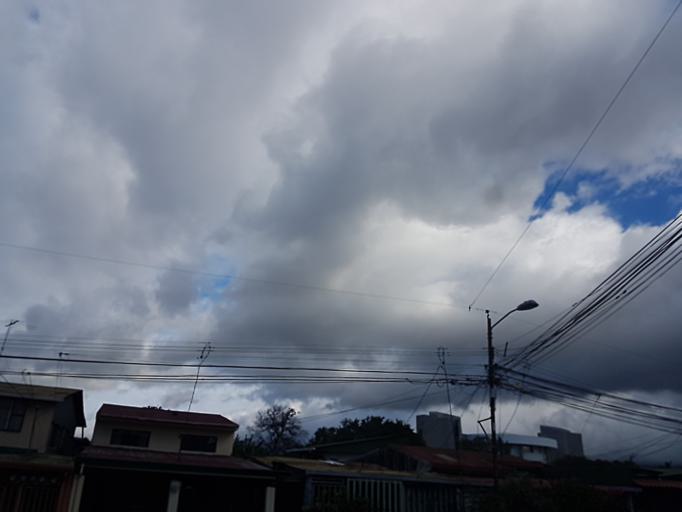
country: CR
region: San Jose
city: San Pedro
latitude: 9.9225
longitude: -84.0530
